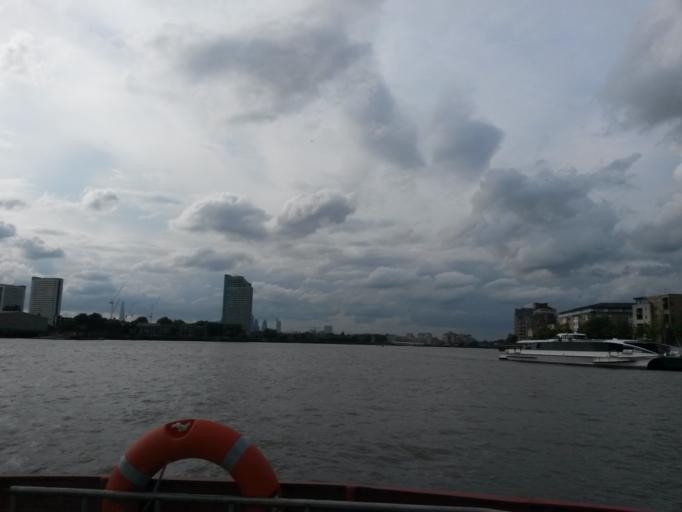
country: GB
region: England
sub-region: Greater London
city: Poplar
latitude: 51.4867
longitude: -0.0221
